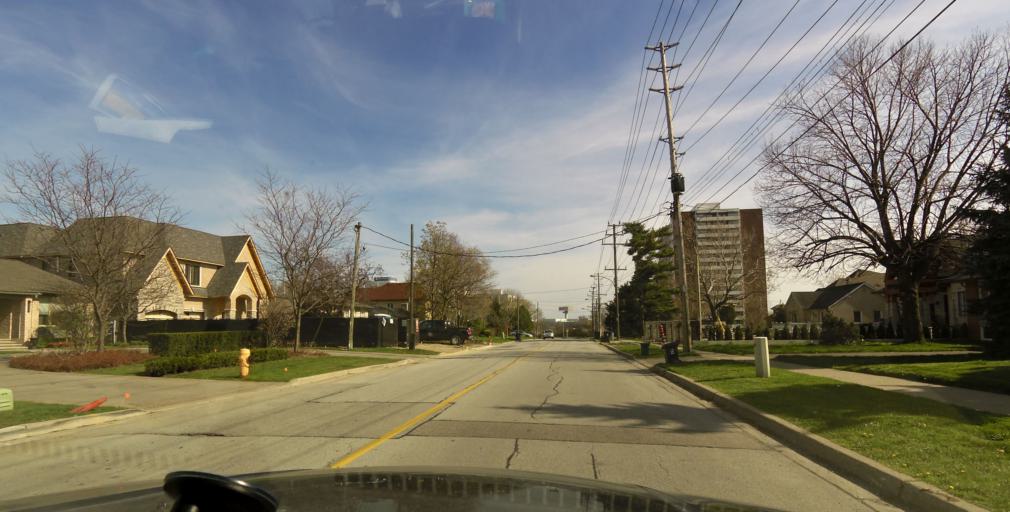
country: CA
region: Ontario
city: Etobicoke
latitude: 43.6298
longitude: -79.5635
